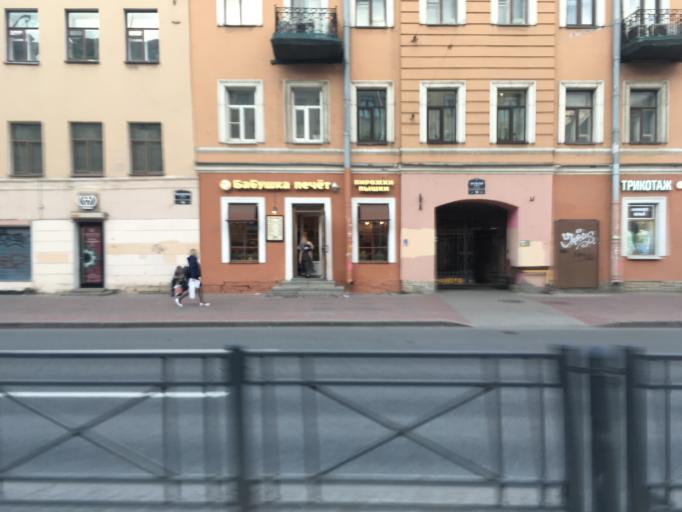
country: RU
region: St.-Petersburg
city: Centralniy
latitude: 59.9202
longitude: 30.3541
